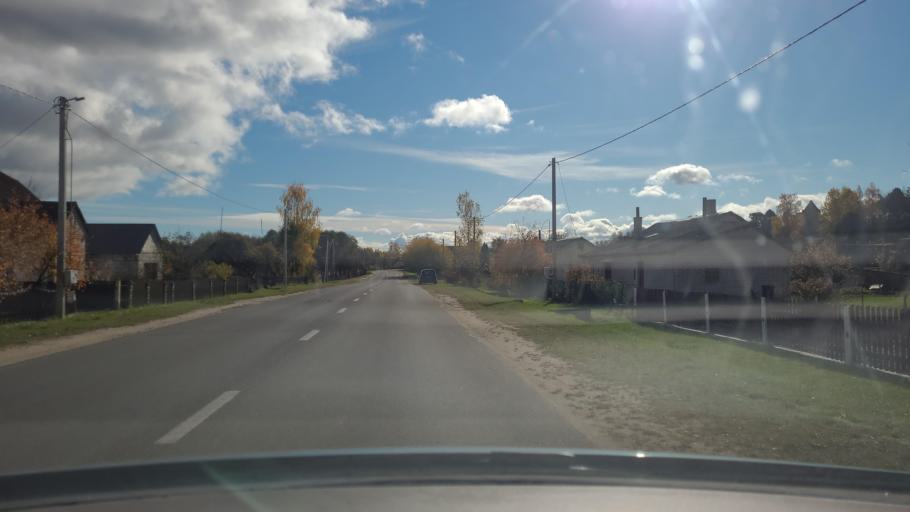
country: BY
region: Grodnenskaya
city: Astravyets
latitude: 54.6147
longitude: 25.9465
